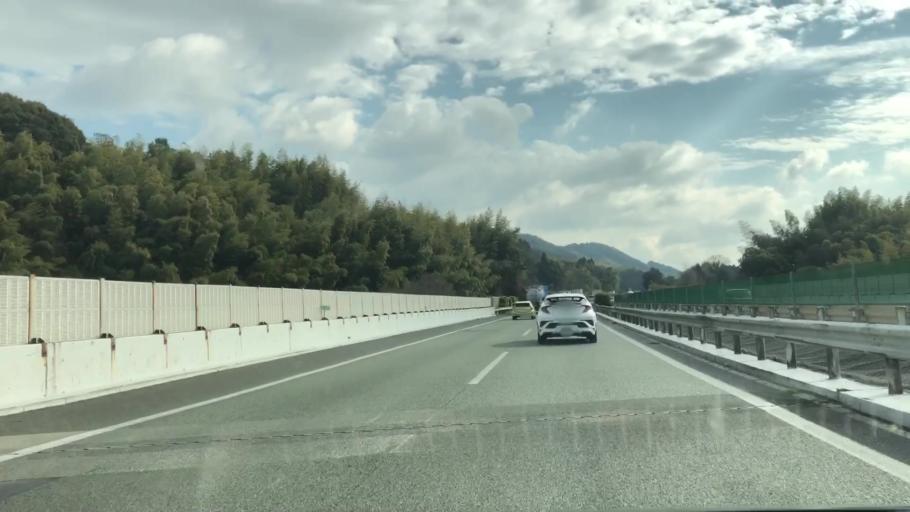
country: JP
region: Fukuoka
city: Setakamachi-takayanagi
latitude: 33.1124
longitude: 130.5309
